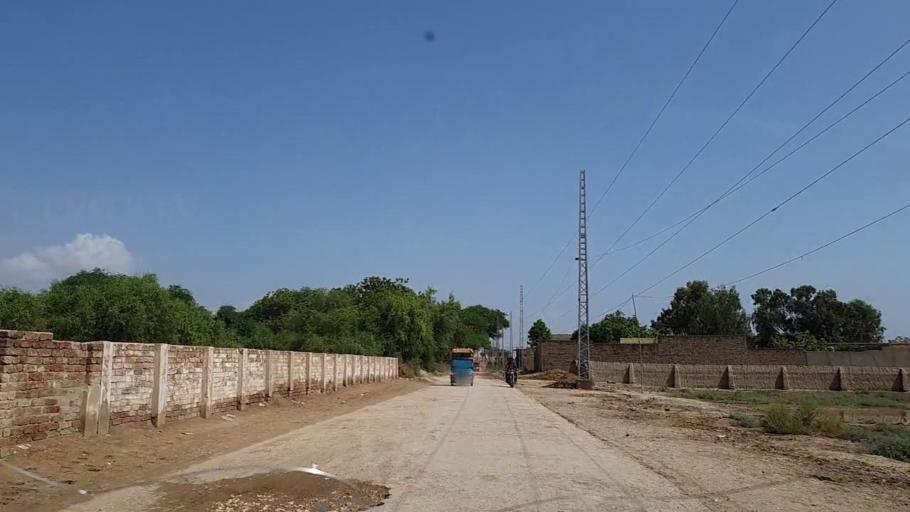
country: PK
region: Sindh
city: Pad Idan
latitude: 26.7797
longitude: 68.2887
